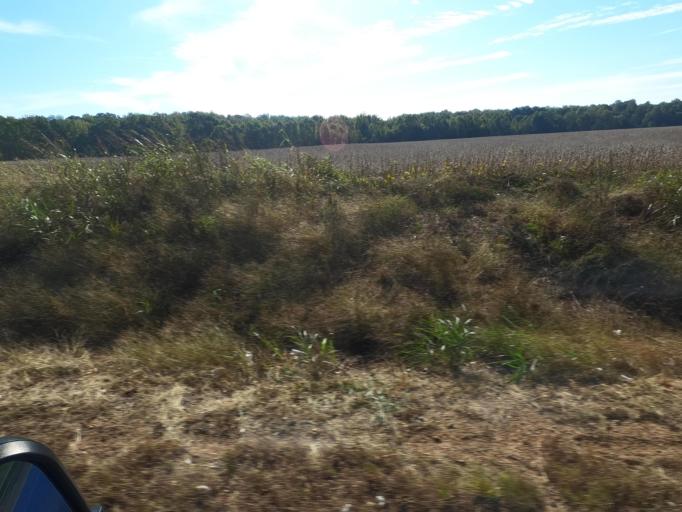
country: US
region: Tennessee
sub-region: Tipton County
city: Munford
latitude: 35.4352
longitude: -89.8002
